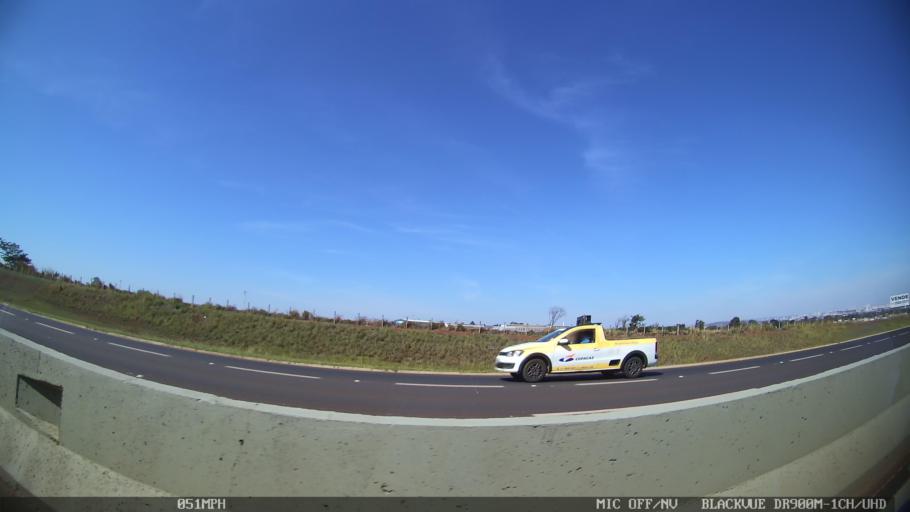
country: BR
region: Sao Paulo
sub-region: Ribeirao Preto
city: Ribeirao Preto
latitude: -21.0959
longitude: -47.7965
